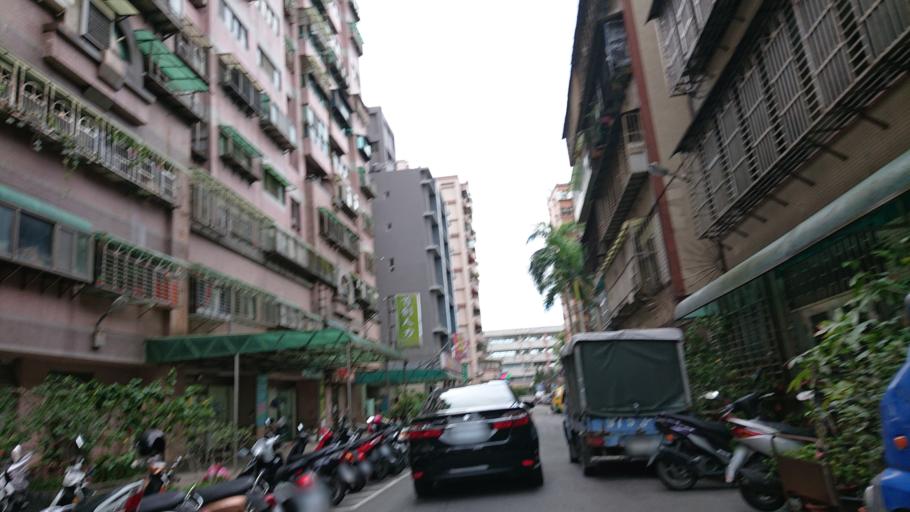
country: TW
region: Taiwan
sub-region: Taoyuan
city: Taoyuan
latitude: 24.9301
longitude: 121.3736
